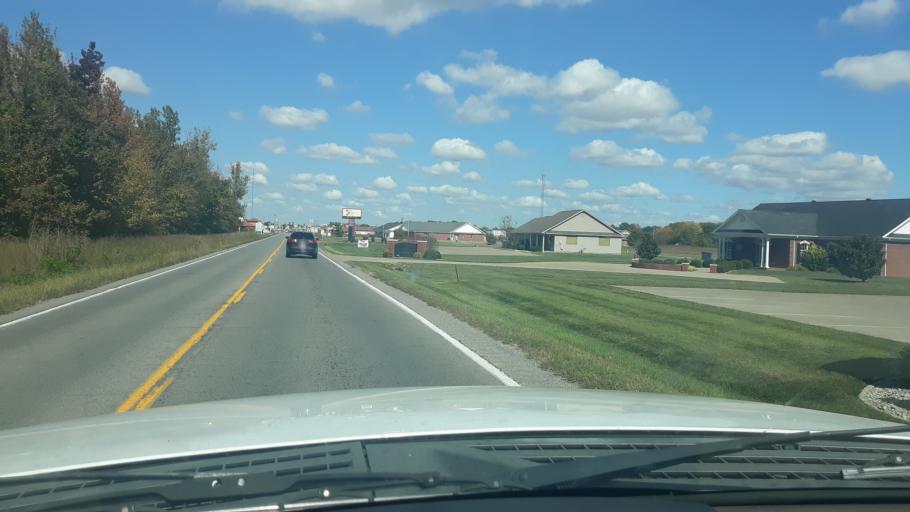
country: US
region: Illinois
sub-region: Saline County
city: Harrisburg
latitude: 37.7220
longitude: -88.5394
